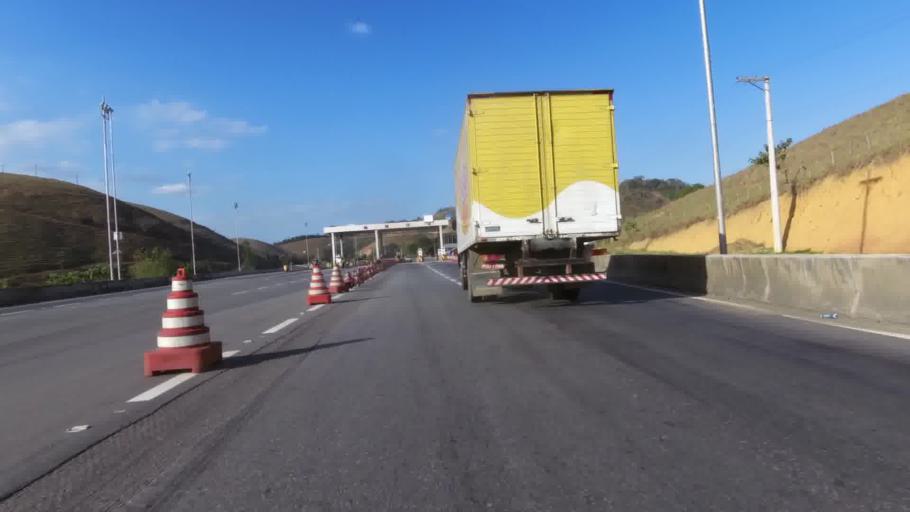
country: BR
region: Espirito Santo
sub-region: Mimoso Do Sul
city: Mimoso do Sul
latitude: -21.1591
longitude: -41.2817
